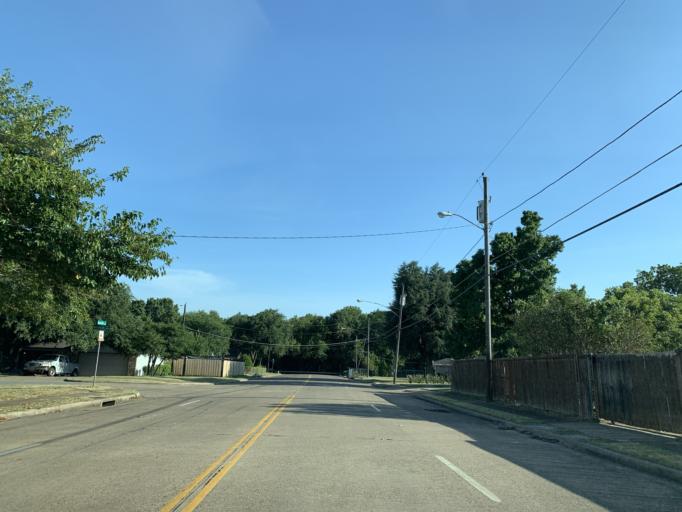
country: US
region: Texas
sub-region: Dallas County
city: Cockrell Hill
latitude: 32.7115
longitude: -96.9001
